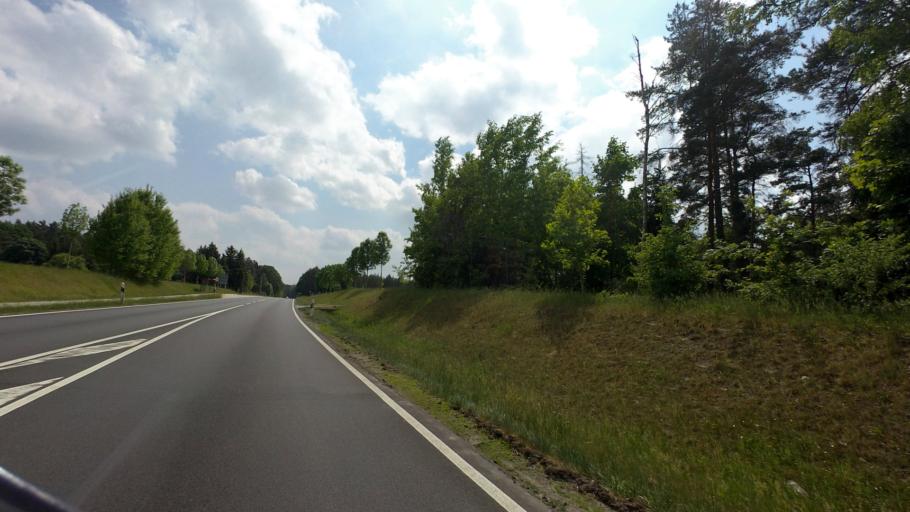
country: DE
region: Saxony
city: Rietschen
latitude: 51.3514
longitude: 14.8029
